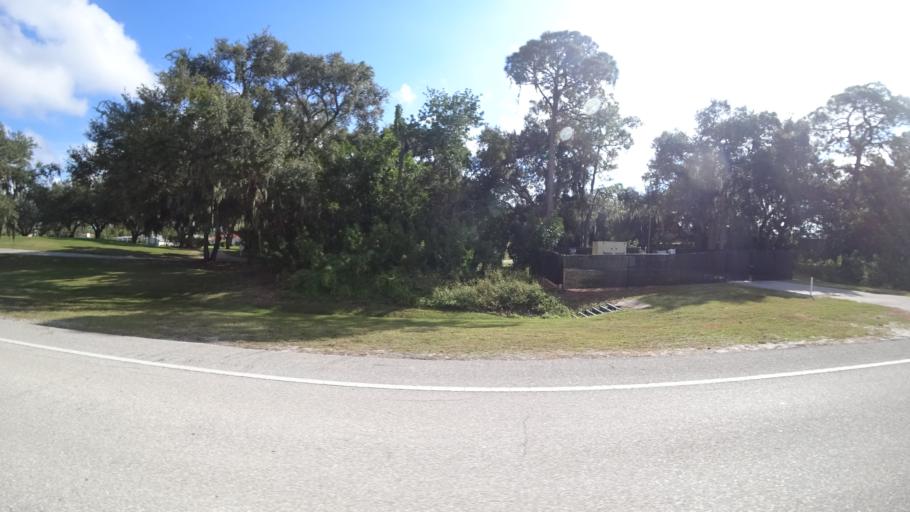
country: US
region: Florida
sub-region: Sarasota County
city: Desoto Lakes
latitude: 27.3986
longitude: -82.4871
